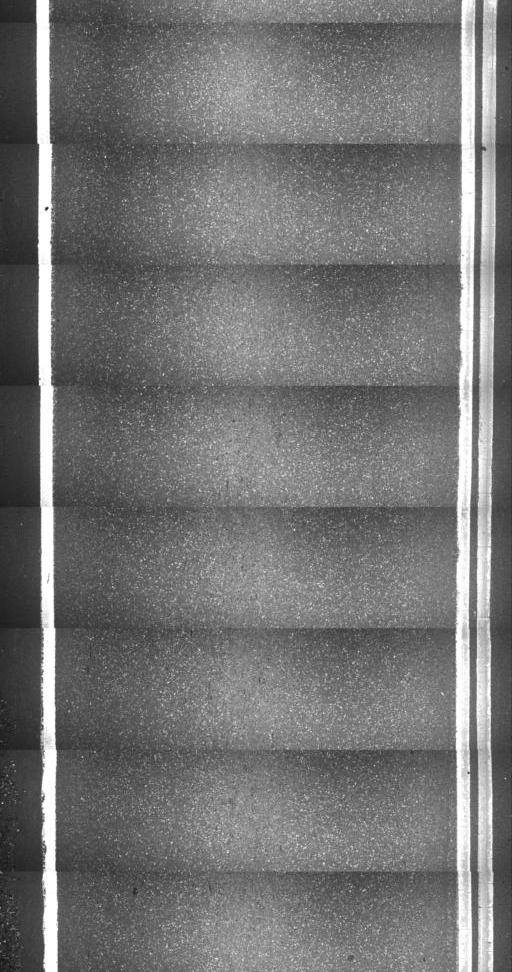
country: US
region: Vermont
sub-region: Washington County
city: South Barre
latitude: 44.1801
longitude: -72.5027
